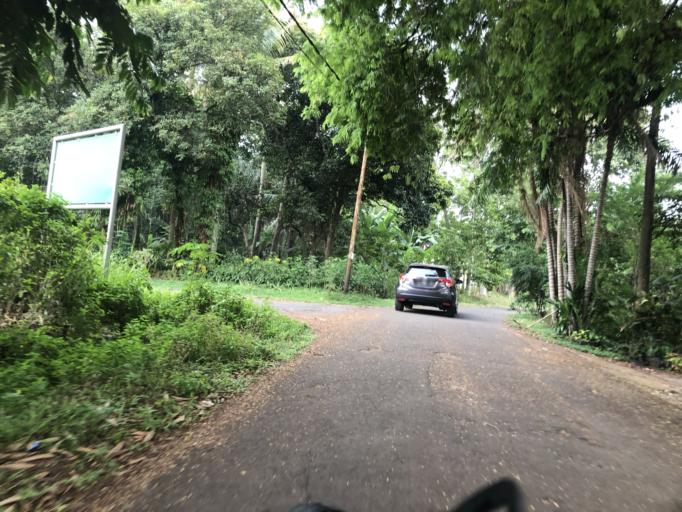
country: ID
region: West Java
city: Ciampea
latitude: -6.5523
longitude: 106.7197
